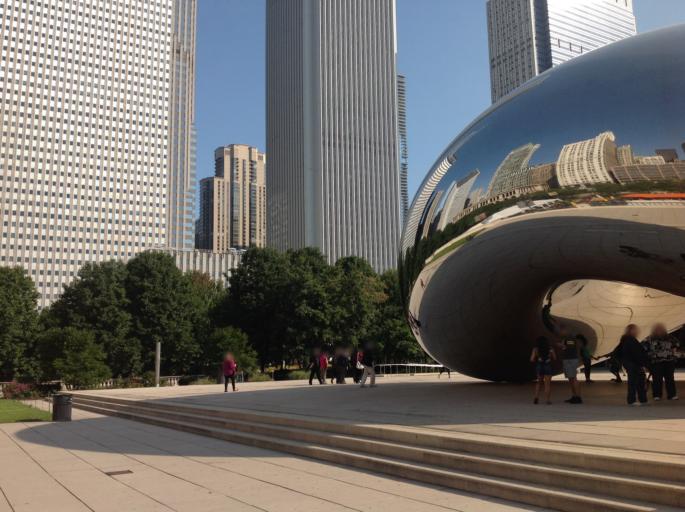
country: US
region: Illinois
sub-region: Cook County
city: Chicago
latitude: 41.8826
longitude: -87.6235
